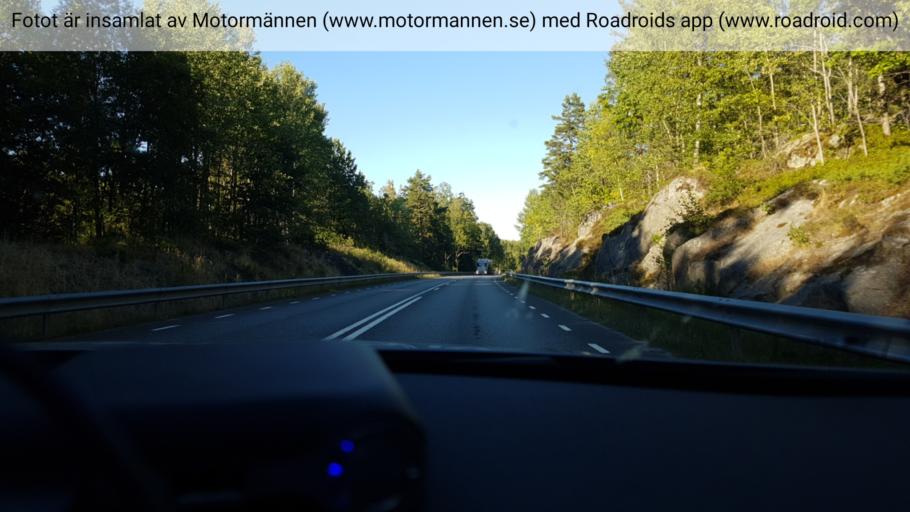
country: SE
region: Joenkoeping
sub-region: Habo Kommun
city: Habo
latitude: 58.0056
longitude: 14.1278
